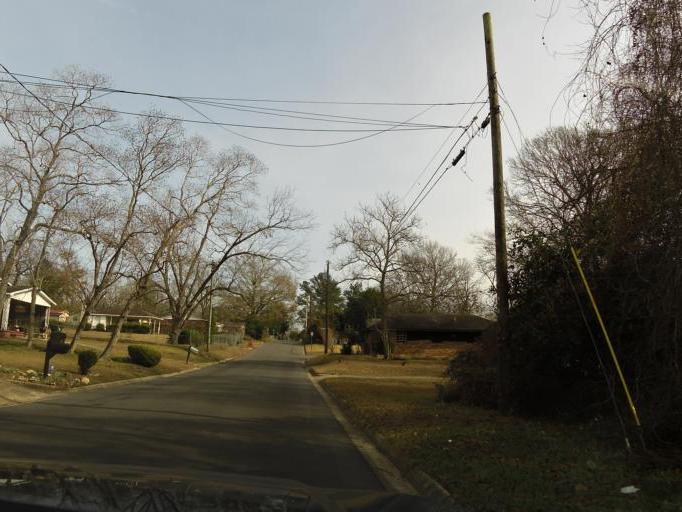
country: US
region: Alabama
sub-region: Houston County
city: Dothan
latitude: 31.2265
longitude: -85.3798
